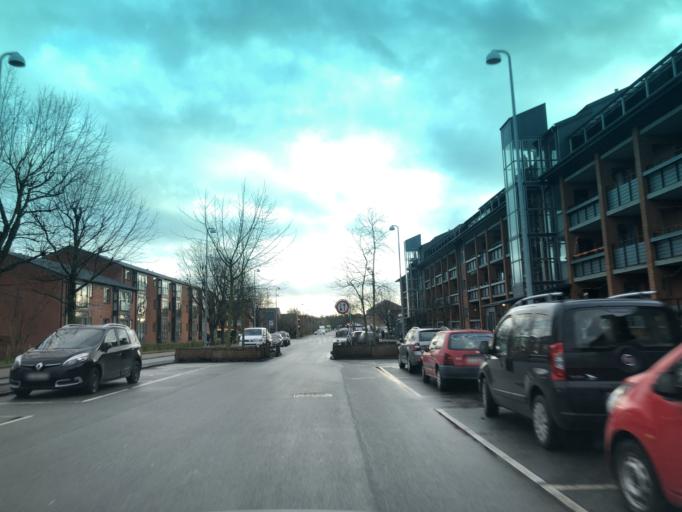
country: DK
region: Capital Region
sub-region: Tarnby Kommune
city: Tarnby
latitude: 55.6353
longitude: 12.6099
